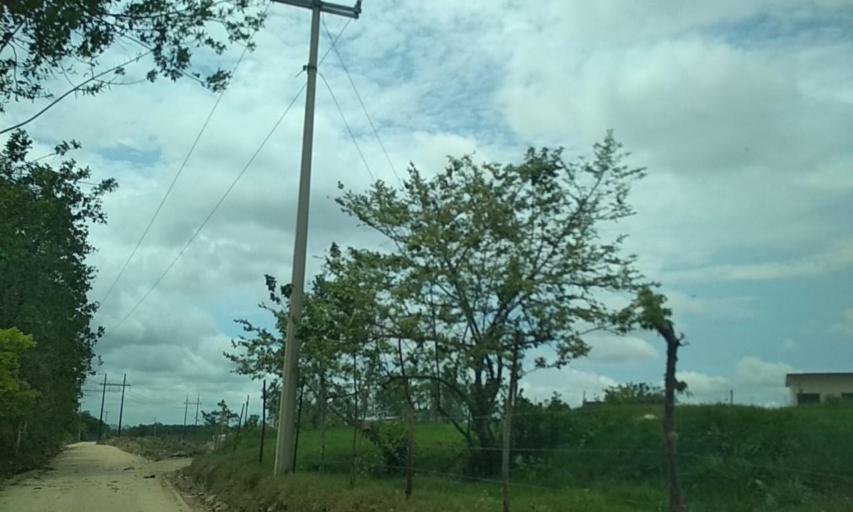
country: MX
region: Veracruz
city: Las Choapas
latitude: 17.8992
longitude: -94.1205
